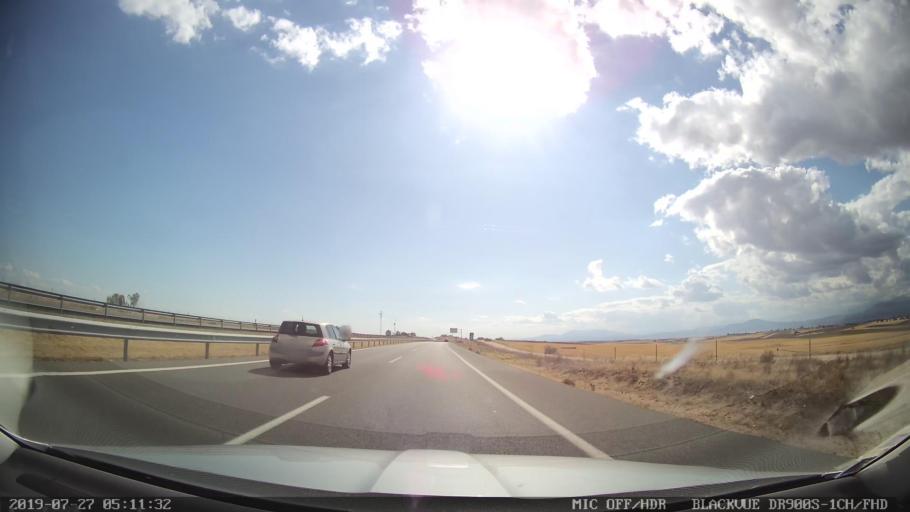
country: ES
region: Castille-La Mancha
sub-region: Province of Toledo
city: Quismondo
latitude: 40.1161
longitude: -4.3030
